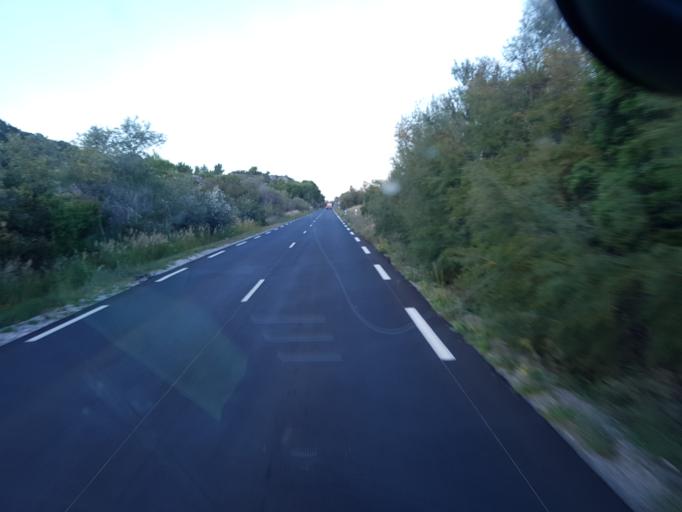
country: FR
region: Languedoc-Roussillon
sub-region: Departement de l'Aude
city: Port-la-Nouvelle
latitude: 42.9916
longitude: 3.0376
